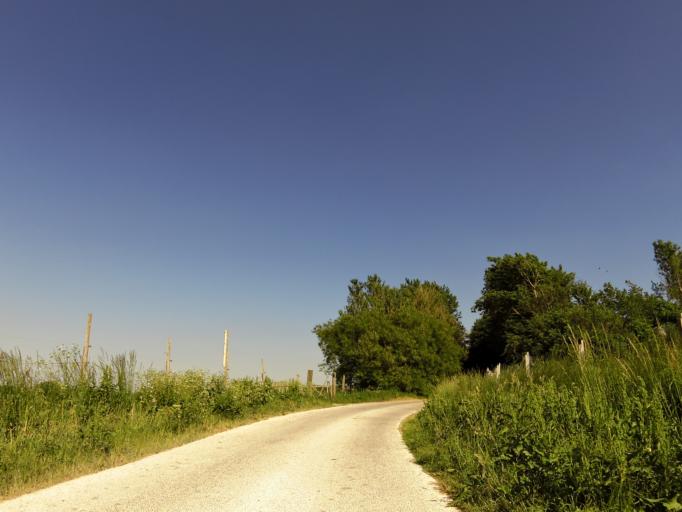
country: DK
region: Central Jutland
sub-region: Holstebro Kommune
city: Vinderup
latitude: 56.4663
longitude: 8.7097
